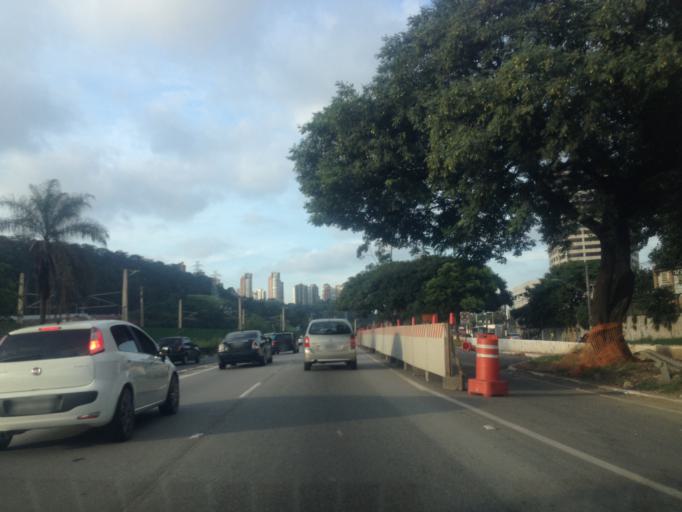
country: BR
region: Sao Paulo
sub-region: Taboao Da Serra
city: Taboao da Serra
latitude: -23.6433
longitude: -46.7251
